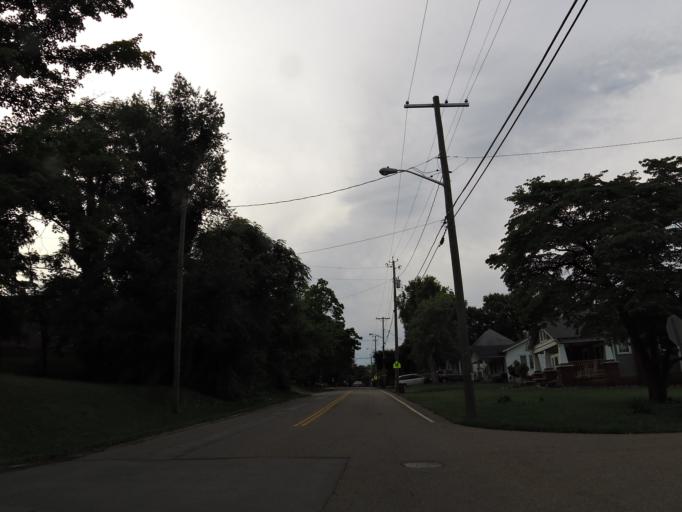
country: US
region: Tennessee
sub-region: Knox County
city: Knoxville
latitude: 35.9954
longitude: -83.9162
